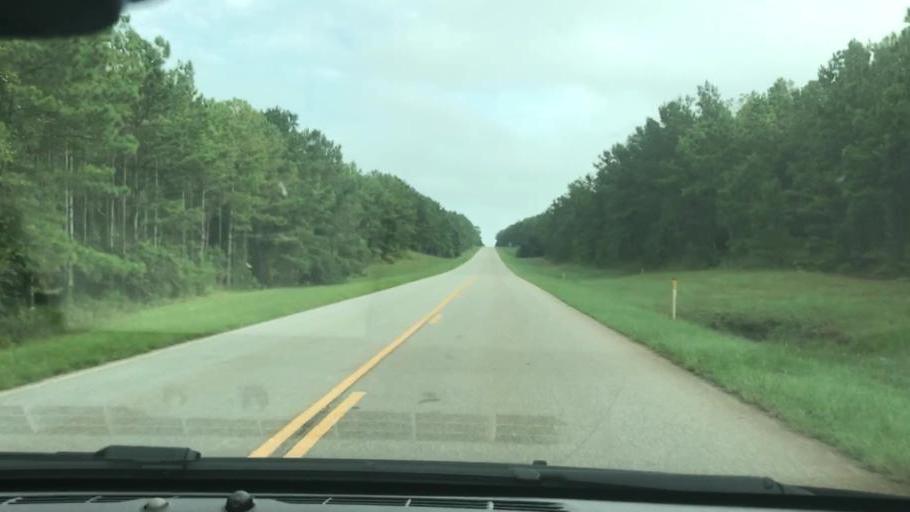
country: US
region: Georgia
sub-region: Stewart County
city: Lumpkin
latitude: 31.9941
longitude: -84.9330
